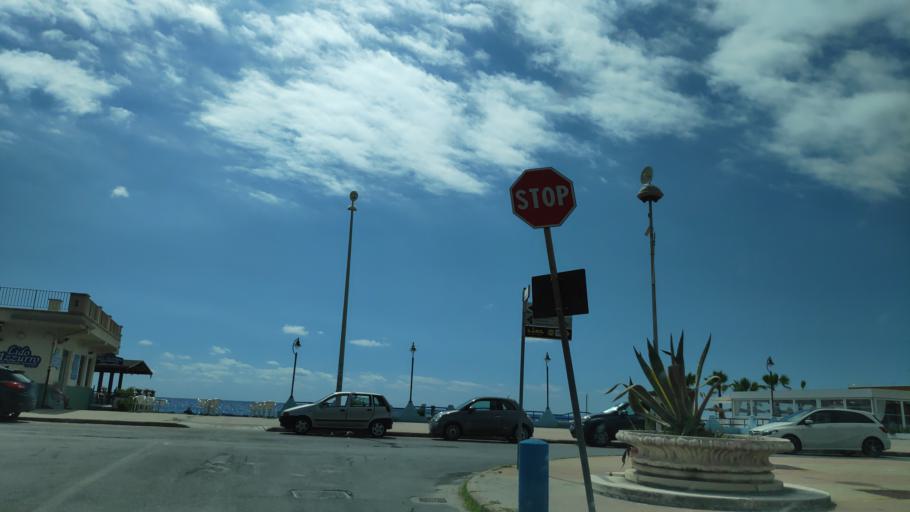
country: IT
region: Calabria
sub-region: Provincia di Cosenza
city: Amantea
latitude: 39.1318
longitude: 16.0692
